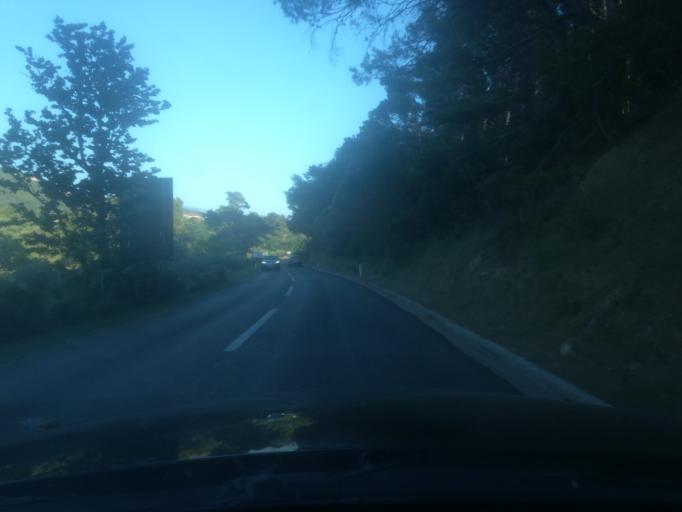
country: HR
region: Primorsko-Goranska
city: Banjol
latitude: 44.7564
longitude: 14.7742
